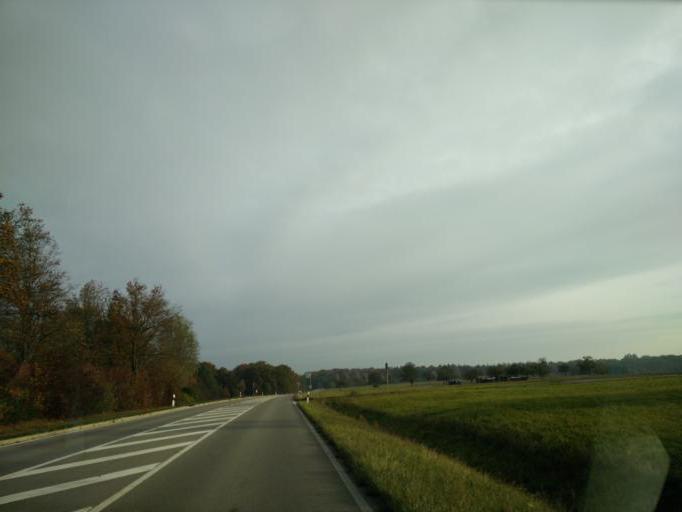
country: DE
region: Baden-Wuerttemberg
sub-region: Tuebingen Region
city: Kusterdingen
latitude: 48.5570
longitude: 9.0980
